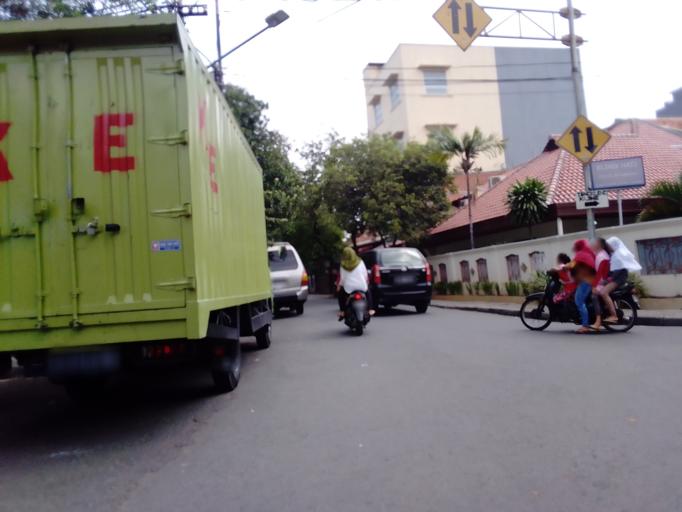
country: ID
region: Jakarta Raya
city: Jakarta
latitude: -6.1792
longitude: 106.8110
